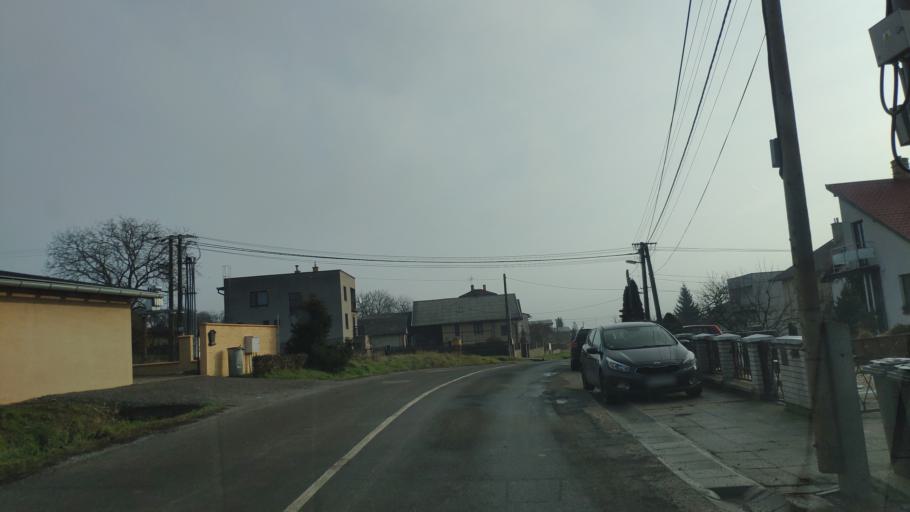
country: SK
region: Kosicky
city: Kosice
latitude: 48.7080
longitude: 21.4017
